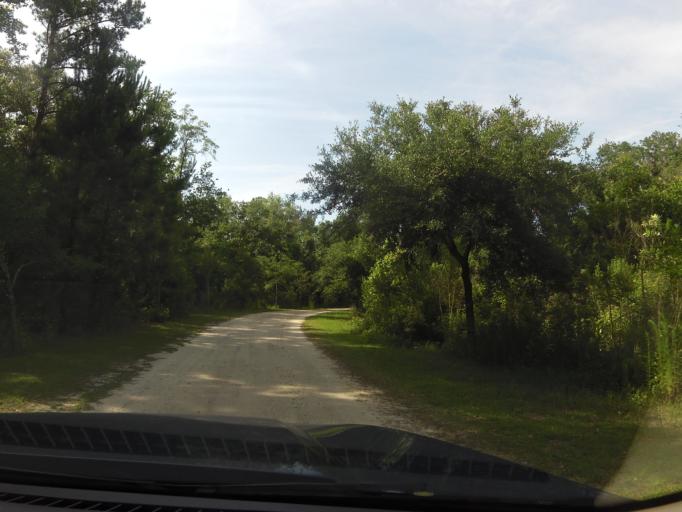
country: US
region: Florida
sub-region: Duval County
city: Atlantic Beach
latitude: 30.4869
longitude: -81.4910
